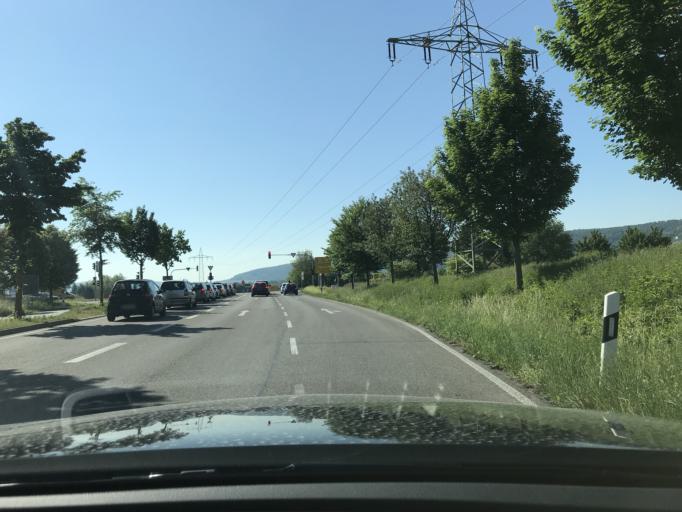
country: DE
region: Baden-Wuerttemberg
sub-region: Regierungsbezirk Stuttgart
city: Fellbach
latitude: 48.8200
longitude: 9.2923
